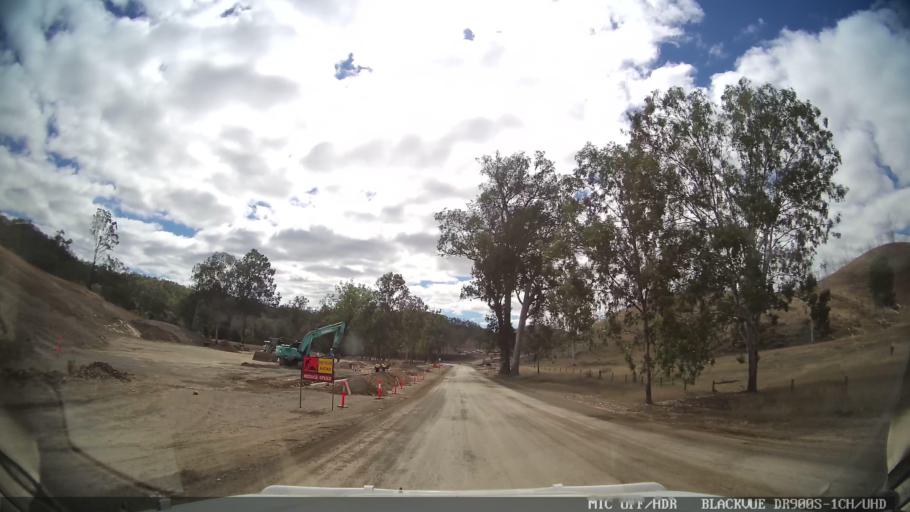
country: AU
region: Queensland
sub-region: Gladstone
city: Toolooa
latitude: -24.6169
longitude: 151.2986
